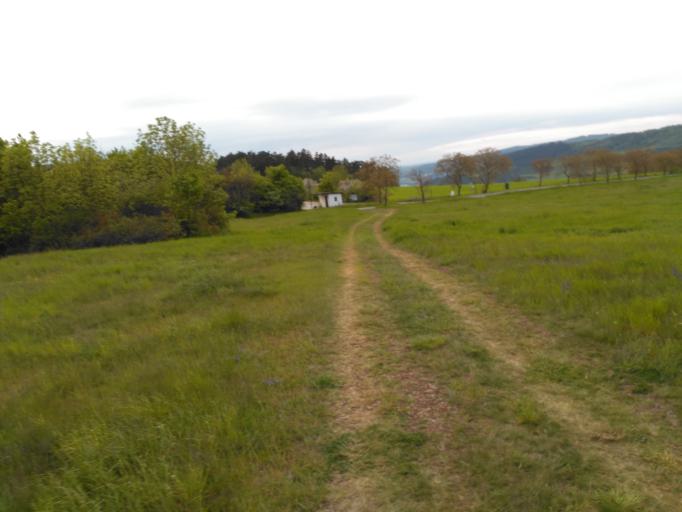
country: CZ
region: Central Bohemia
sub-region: Okres Beroun
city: Beroun
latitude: 49.9151
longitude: 14.0759
